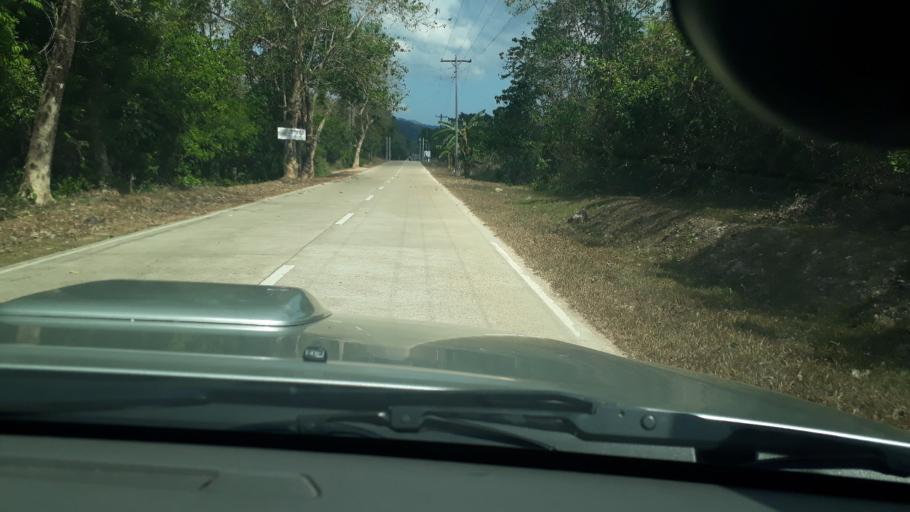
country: PH
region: Mimaropa
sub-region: Province of Palawan
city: Salvacion
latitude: 12.1254
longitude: 119.9384
